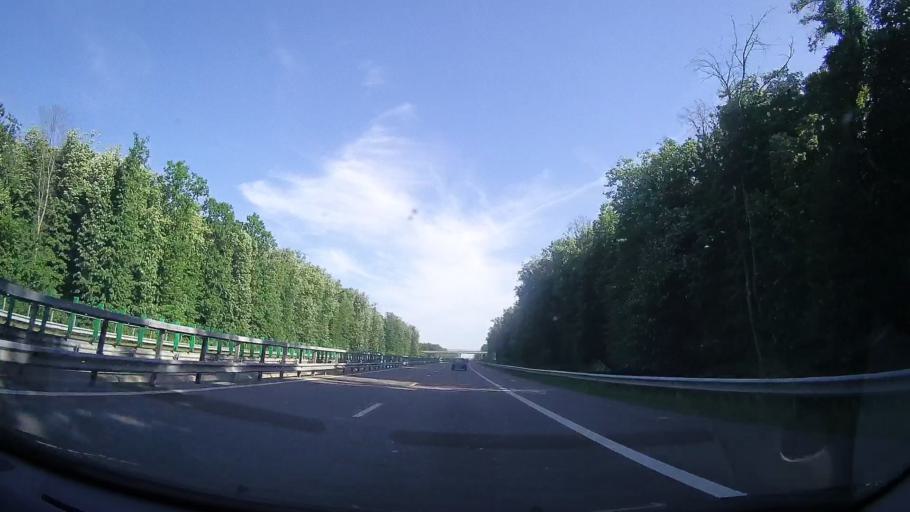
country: RO
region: Prahova
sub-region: Comuna Rafov
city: Buda
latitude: 44.8478
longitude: 26.2064
